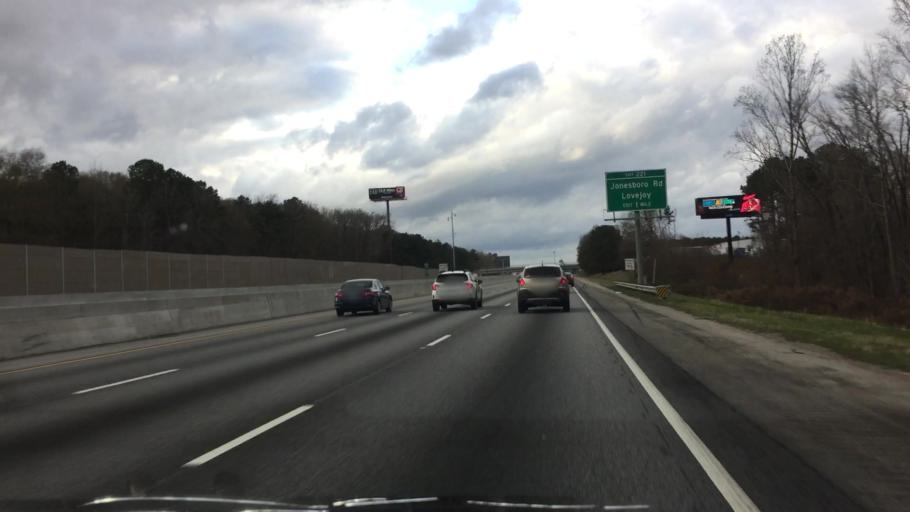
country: US
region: Georgia
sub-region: Henry County
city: McDonough
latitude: 33.4467
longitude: -84.1990
